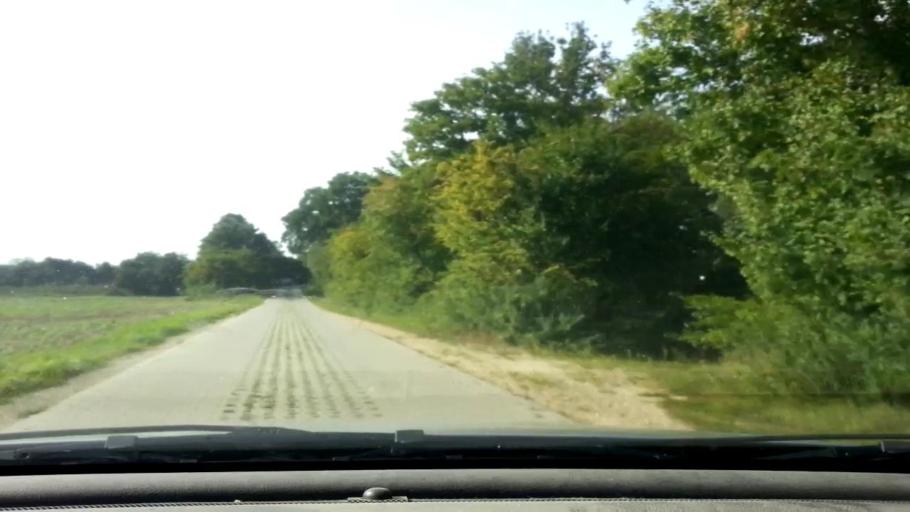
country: DE
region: Bavaria
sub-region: Upper Franconia
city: Strullendorf
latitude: 49.8438
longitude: 10.9489
